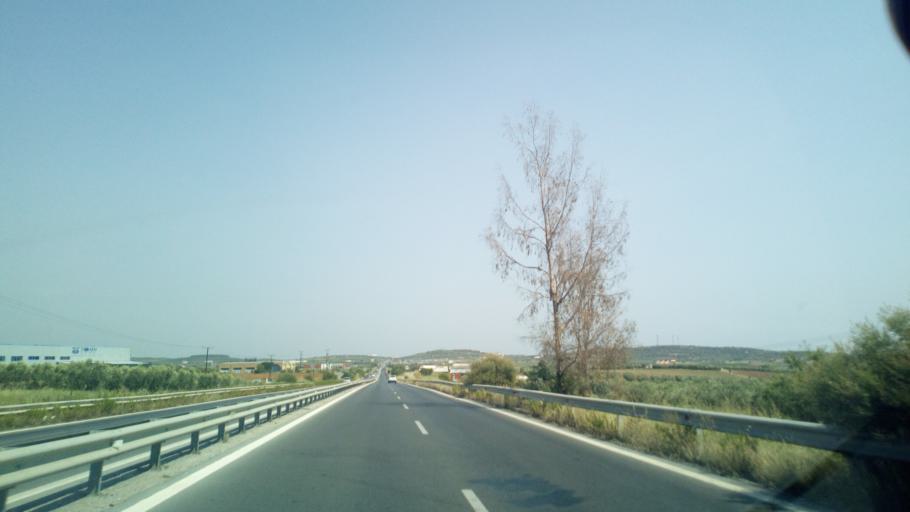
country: GR
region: Central Macedonia
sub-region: Nomos Chalkidikis
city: Nea Flogita
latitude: 40.2637
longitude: 23.2476
